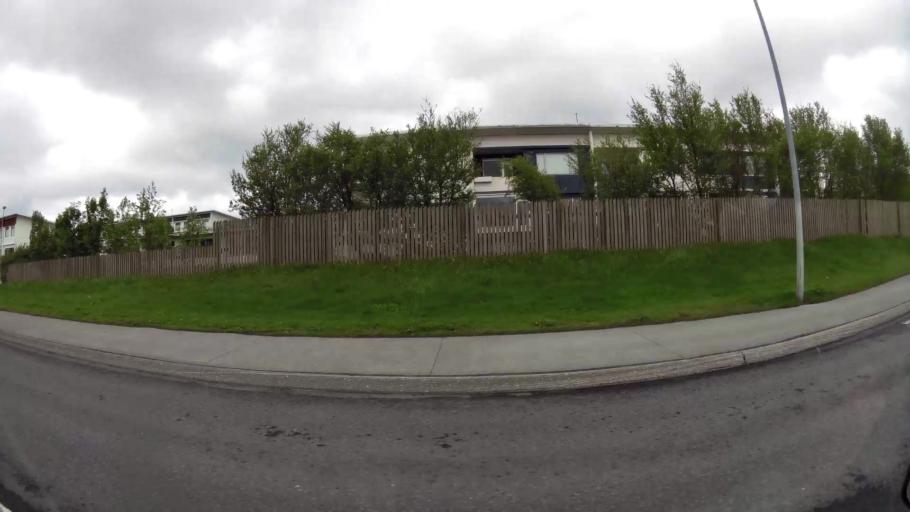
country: IS
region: Capital Region
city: Reykjavik
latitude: 64.1214
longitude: -21.8659
